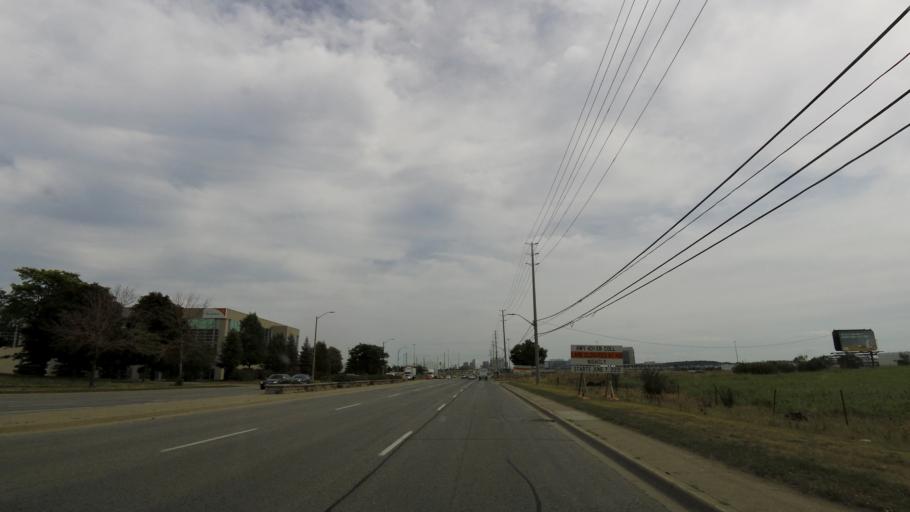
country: CA
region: Ontario
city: Mississauga
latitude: 43.6344
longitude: -79.6907
